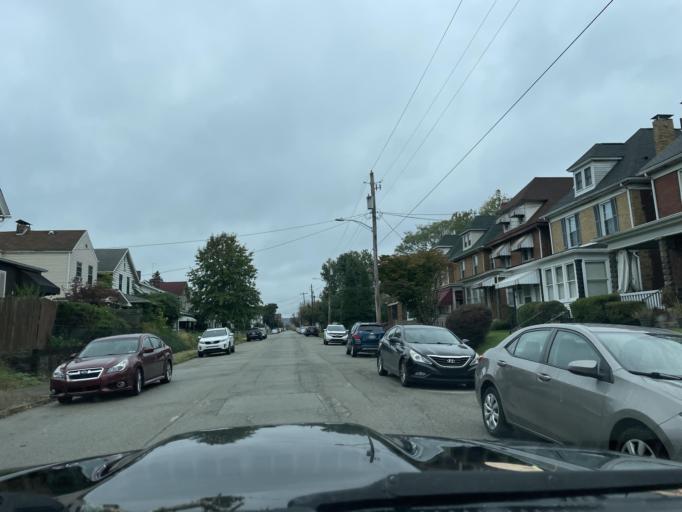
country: US
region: Pennsylvania
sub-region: Westmoreland County
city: Lower Burrell
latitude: 40.5576
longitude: -79.7644
